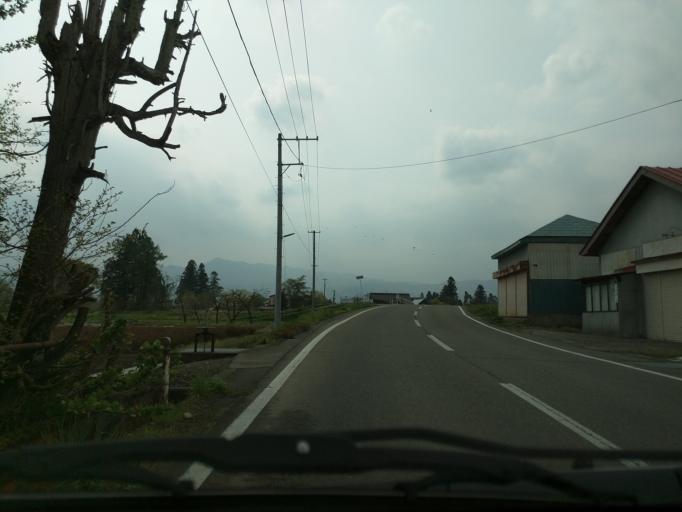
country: JP
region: Fukushima
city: Kitakata
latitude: 37.4413
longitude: 139.8533
